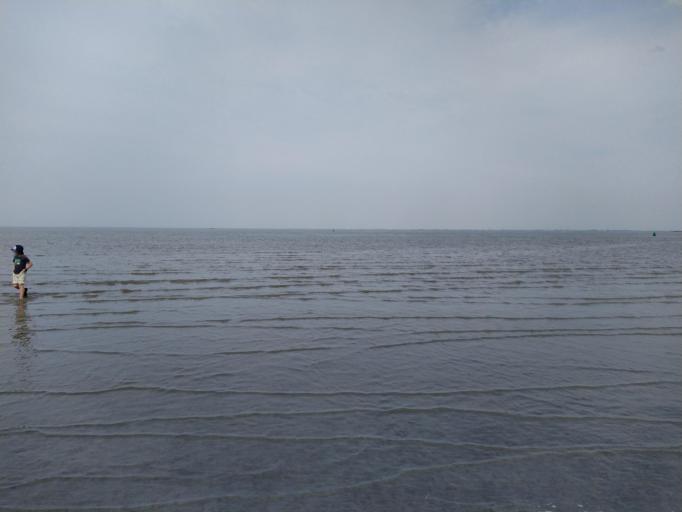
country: DE
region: Lower Saxony
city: Otterndorf
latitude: 53.8337
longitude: 8.8913
